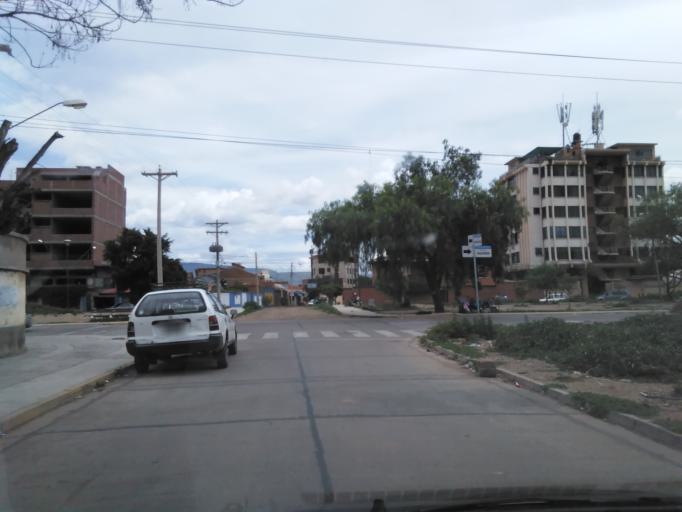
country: BO
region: Cochabamba
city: Cochabamba
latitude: -17.4068
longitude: -66.1690
